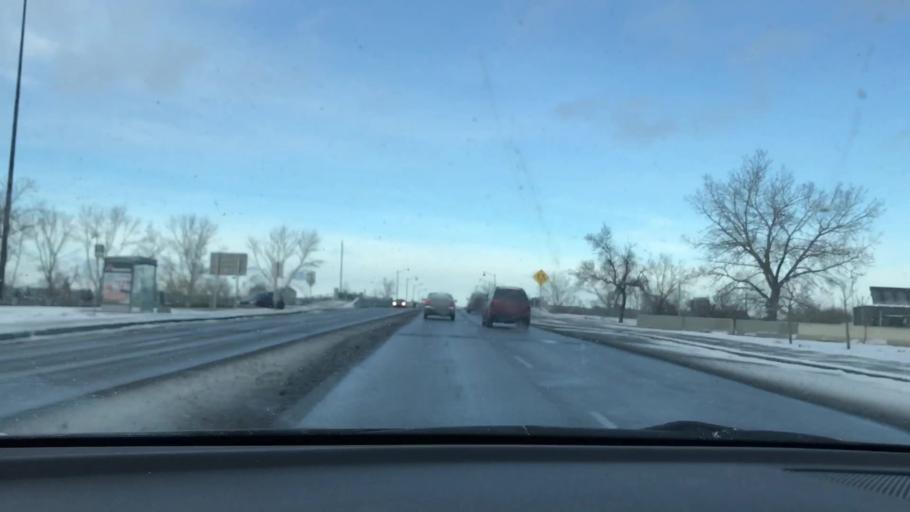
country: CA
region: Alberta
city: Calgary
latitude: 51.0459
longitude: -114.0947
